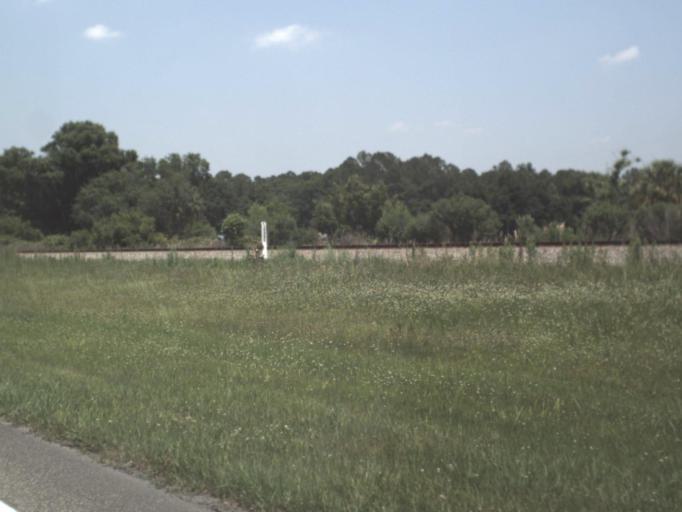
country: US
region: Florida
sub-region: Bradford County
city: Starke
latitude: 30.0387
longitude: -82.0739
